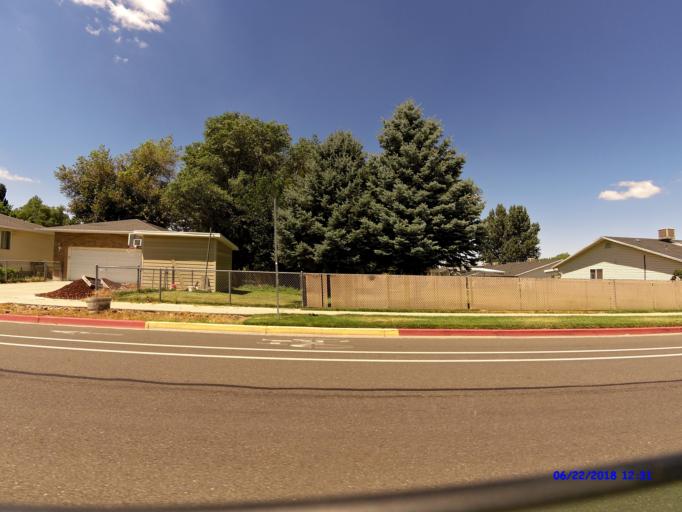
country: US
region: Utah
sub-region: Weber County
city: Ogden
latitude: 41.2389
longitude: -111.9529
